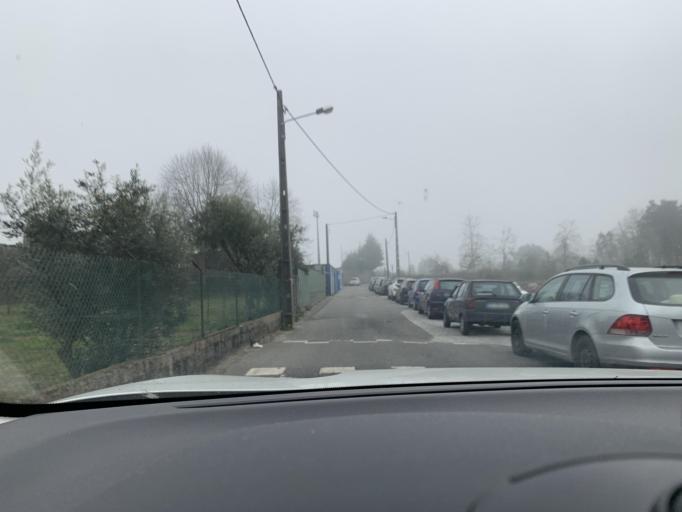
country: PT
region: Viseu
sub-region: Viseu
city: Viseu
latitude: 40.6349
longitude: -7.9203
